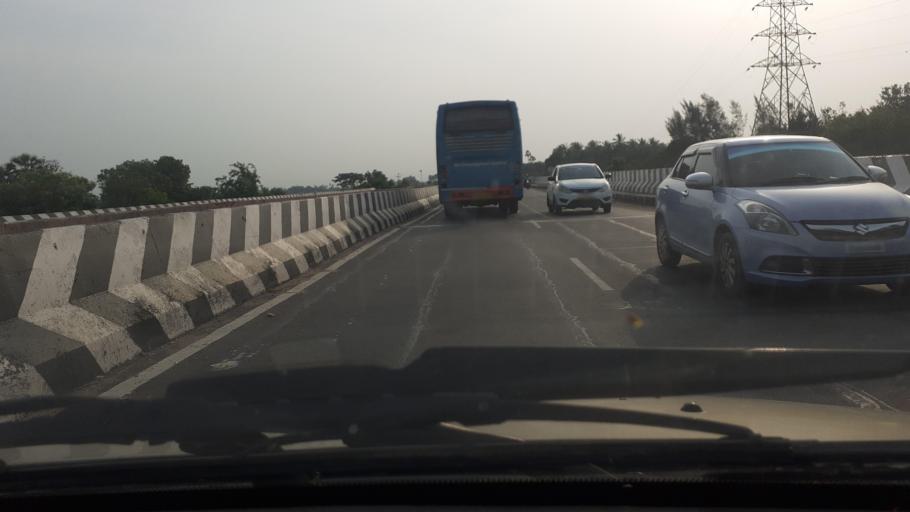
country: IN
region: Tamil Nadu
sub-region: Thoothukkudi
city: Srivaikuntam
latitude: 8.7130
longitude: 77.8359
